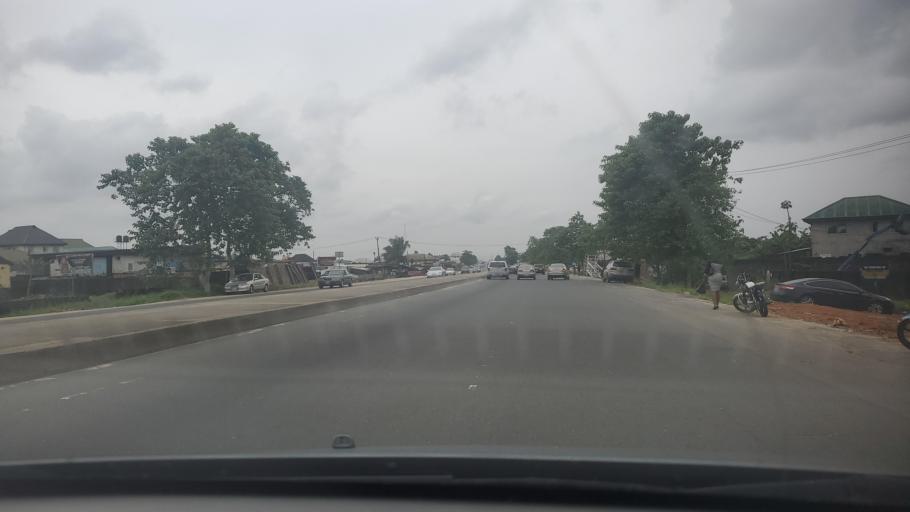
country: NG
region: Rivers
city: Port Harcourt
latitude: 4.8712
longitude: 6.9656
